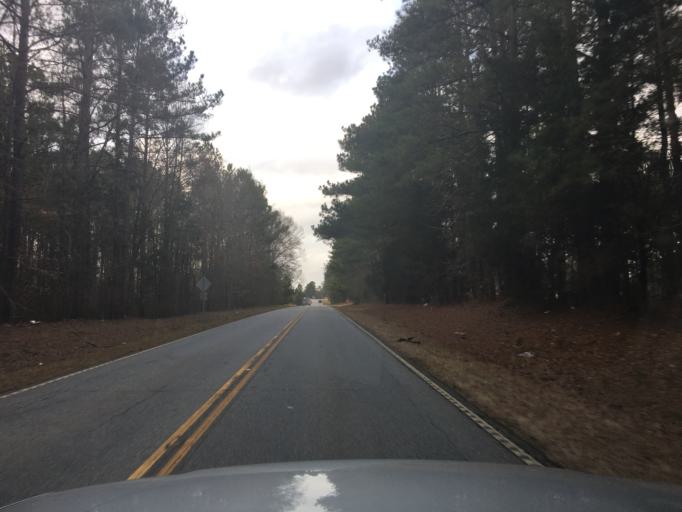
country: US
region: South Carolina
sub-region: Abbeville County
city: Abbeville
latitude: 34.2174
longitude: -82.3902
